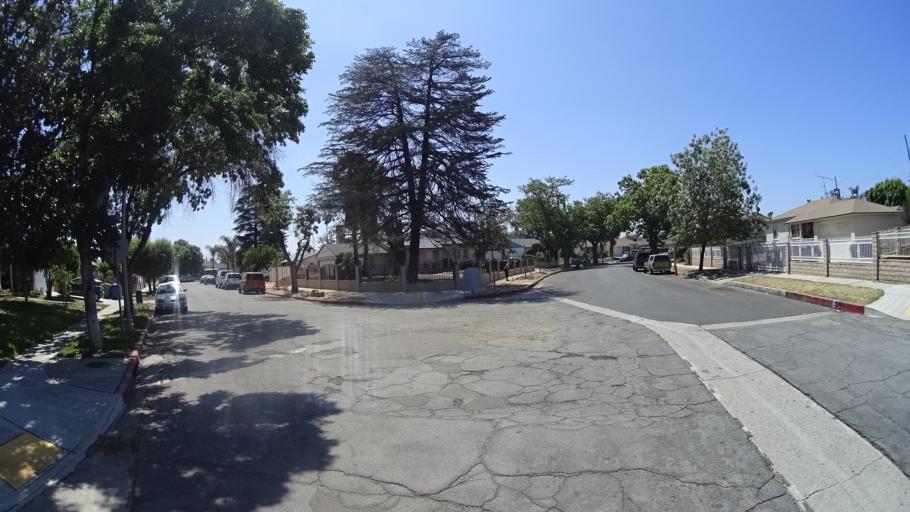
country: US
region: California
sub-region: Los Angeles County
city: Van Nuys
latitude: 34.2324
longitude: -118.4478
